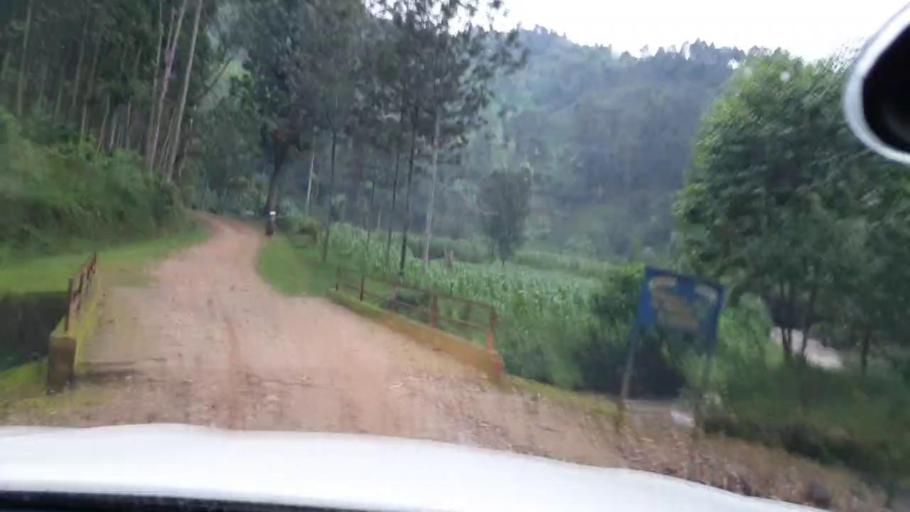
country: RW
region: Western Province
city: Cyangugu
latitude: -2.4113
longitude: 29.1931
